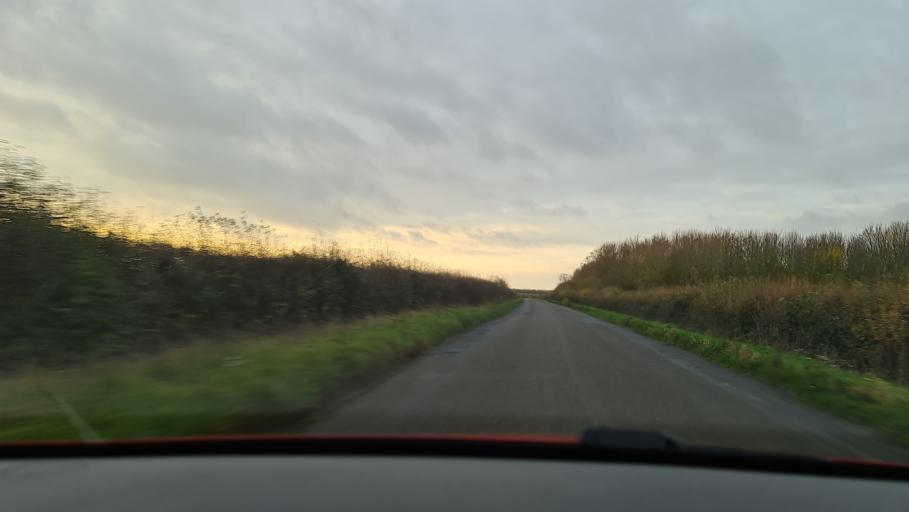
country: GB
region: England
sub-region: Oxfordshire
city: Somerton
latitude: 51.8999
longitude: -1.2747
